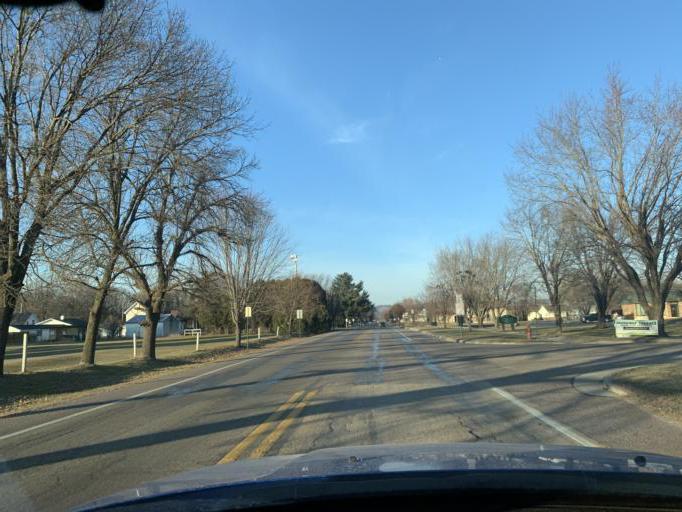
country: US
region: Wisconsin
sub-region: Sauk County
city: Spring Green
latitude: 43.1708
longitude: -90.0640
